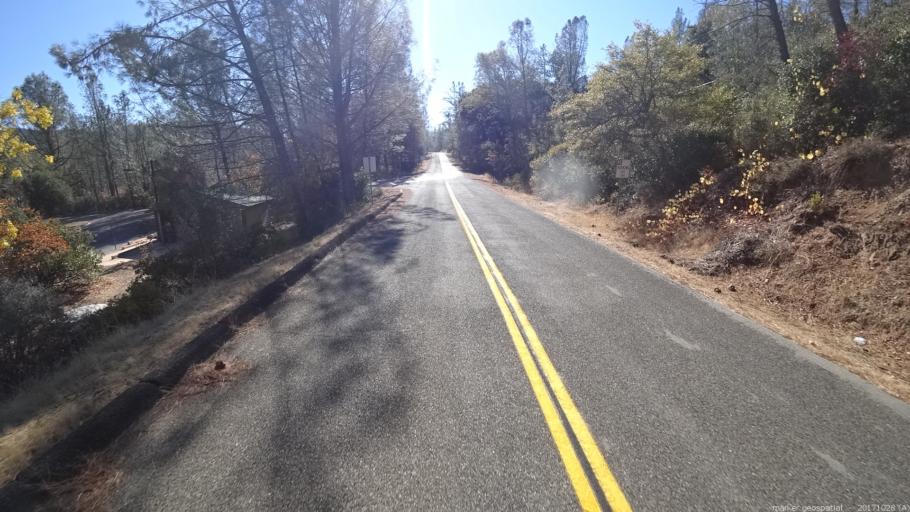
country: US
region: California
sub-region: Shasta County
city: Shasta
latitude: 40.6486
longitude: -122.5580
